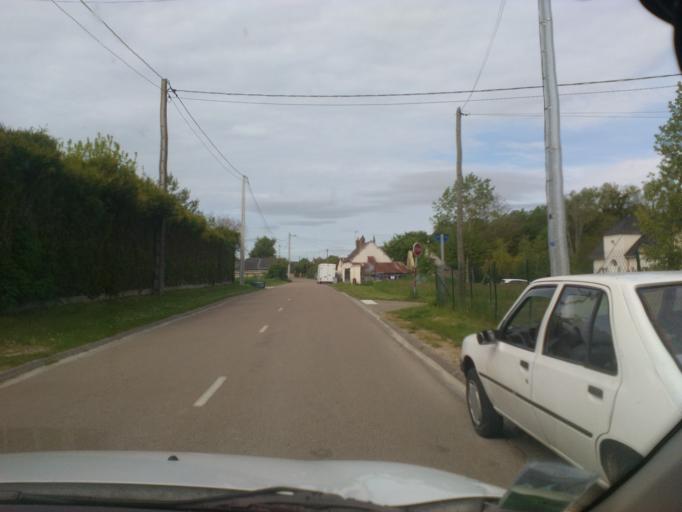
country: FR
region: Champagne-Ardenne
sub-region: Departement de l'Aube
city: Marigny-le-Chatel
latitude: 48.3504
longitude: 3.6455
